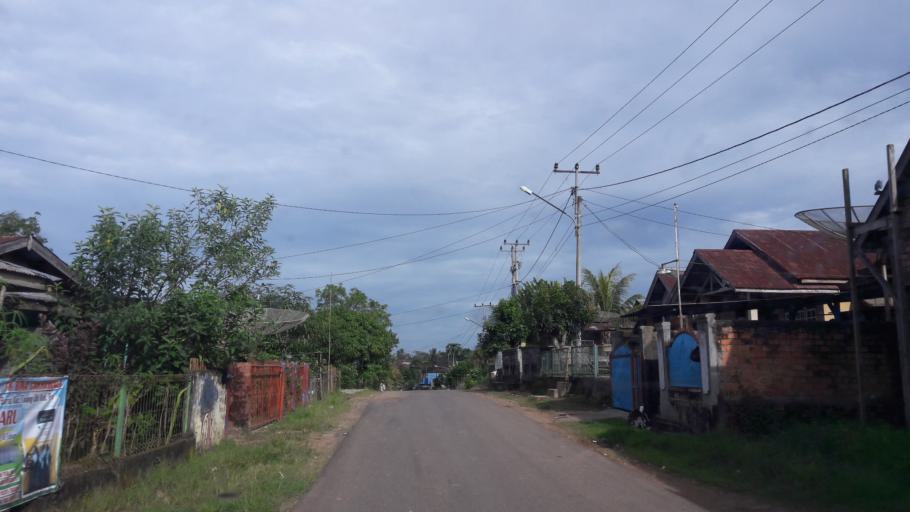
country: ID
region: South Sumatra
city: Gunungmegang Dalam
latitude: -3.2674
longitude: 103.8107
